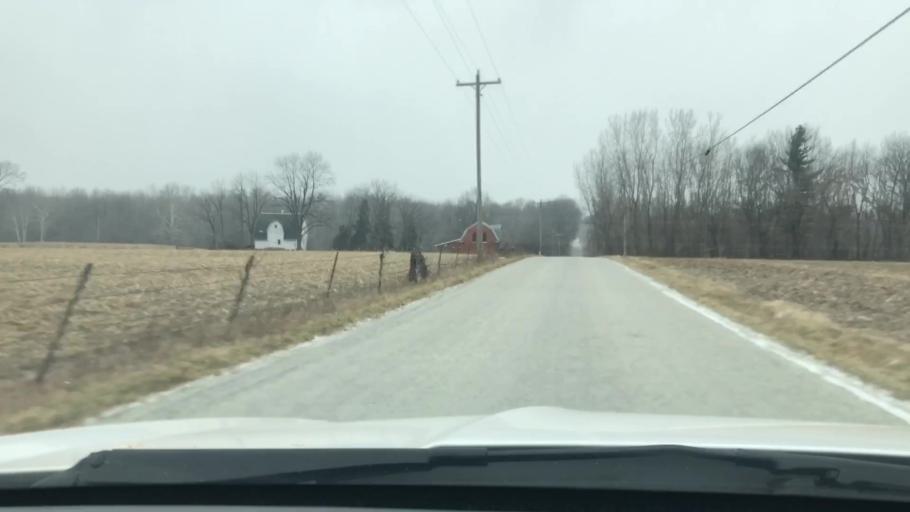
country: US
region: Indiana
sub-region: Fulton County
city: Akron
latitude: 41.0415
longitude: -86.0570
